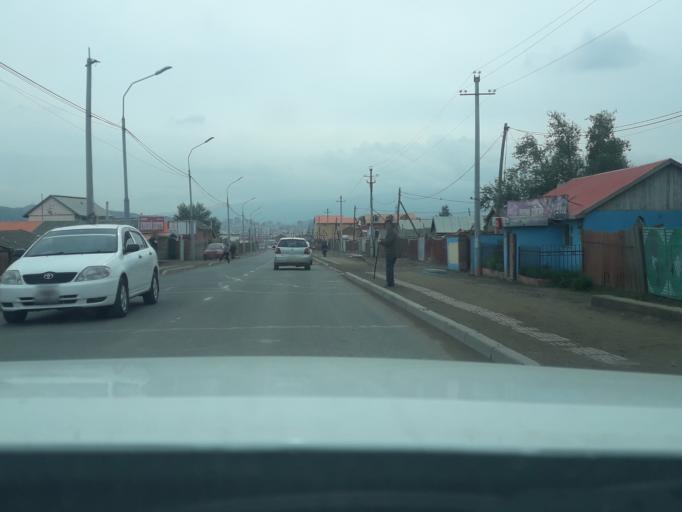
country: MN
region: Ulaanbaatar
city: Ulaanbaatar
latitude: 47.9543
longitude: 106.9052
